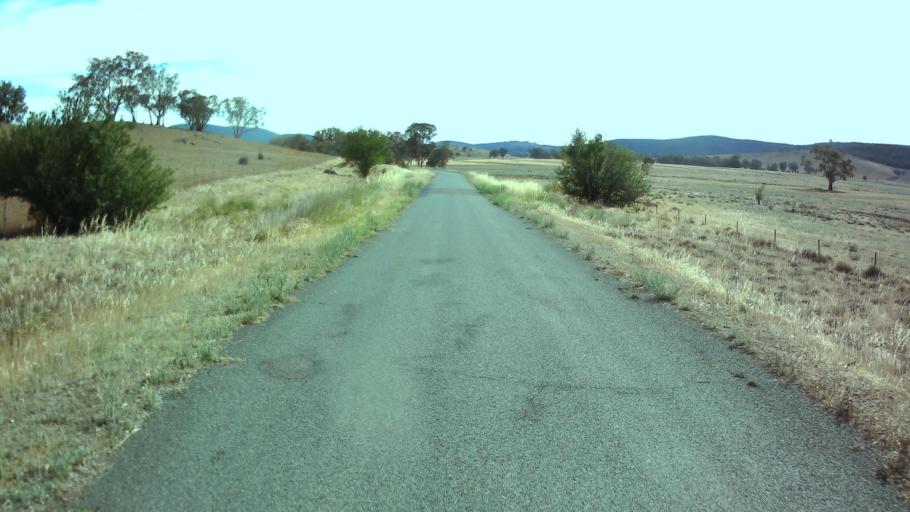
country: AU
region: New South Wales
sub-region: Weddin
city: Grenfell
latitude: -33.8252
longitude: 148.2871
